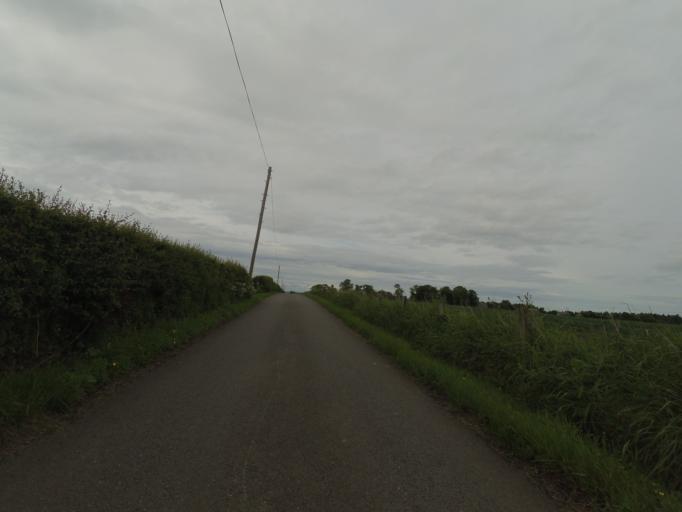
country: GB
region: Scotland
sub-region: East Lothian
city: Macmerry
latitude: 55.9427
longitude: -2.9164
